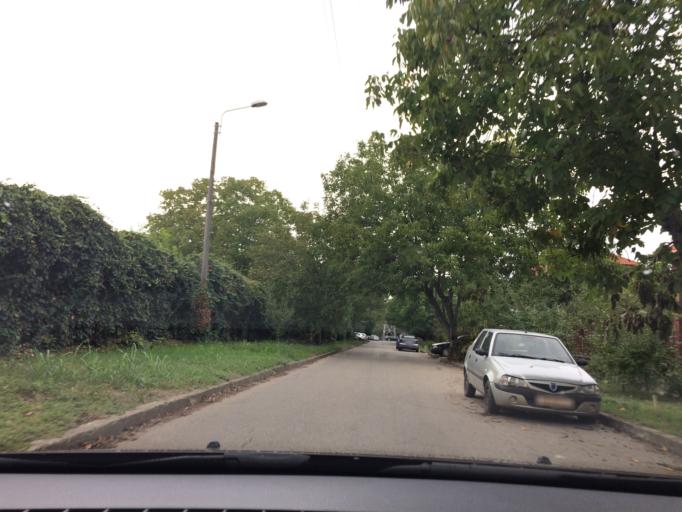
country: RO
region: Timis
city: Timisoara
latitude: 45.7546
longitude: 21.2113
